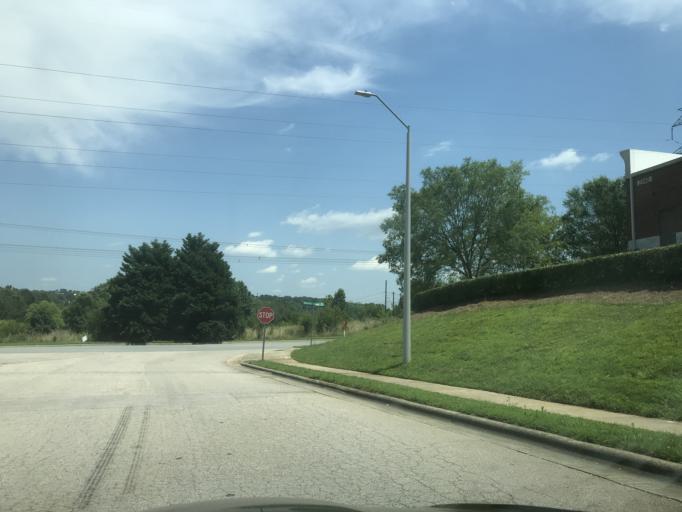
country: US
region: North Carolina
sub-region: Wake County
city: Wake Forest
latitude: 35.9419
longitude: -78.5582
